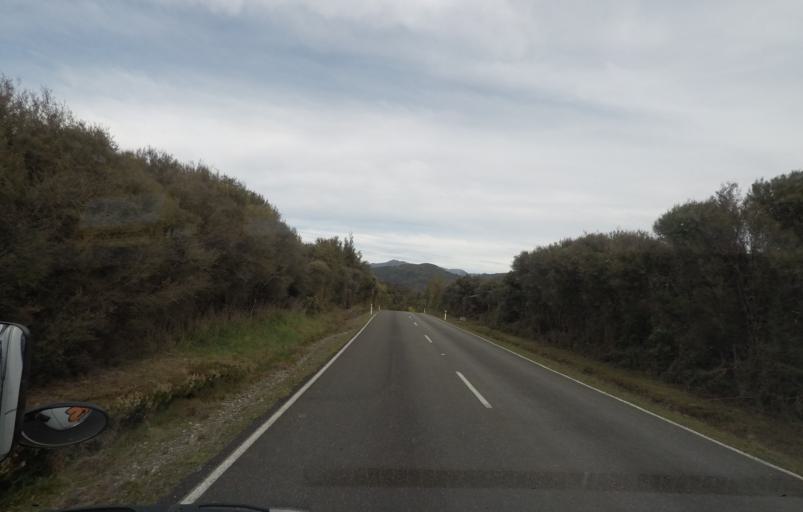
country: NZ
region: Tasman
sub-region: Tasman District
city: Takaka
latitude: -40.8453
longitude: 172.7739
